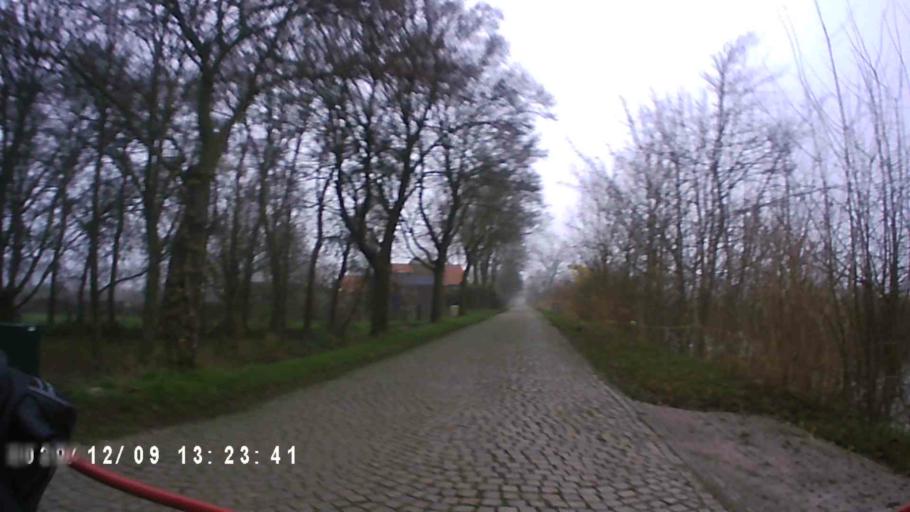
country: NL
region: Groningen
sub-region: Gemeente Bedum
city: Bedum
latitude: 53.2671
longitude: 6.5984
